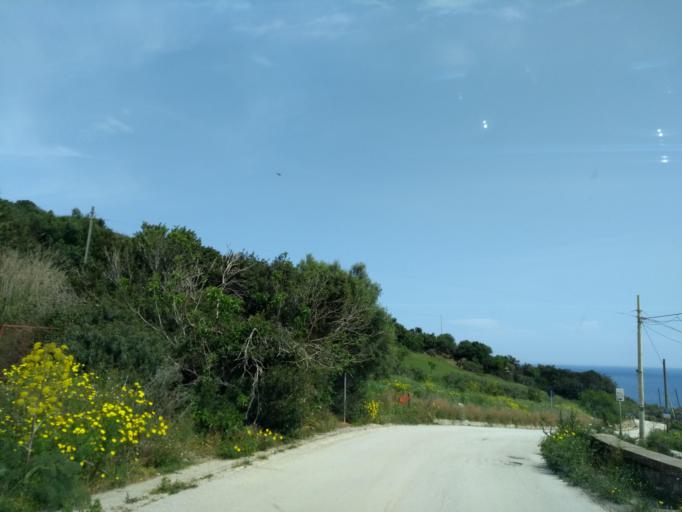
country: IT
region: Sicily
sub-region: Trapani
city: Castelluzzo
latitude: 38.0797
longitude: 12.8069
